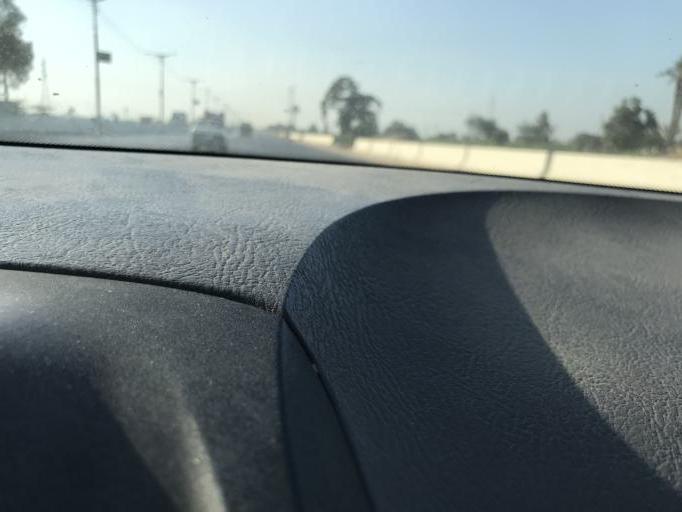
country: EG
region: Muhafazat al Minufiyah
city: Quwaysina
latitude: 30.5189
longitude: 31.1553
